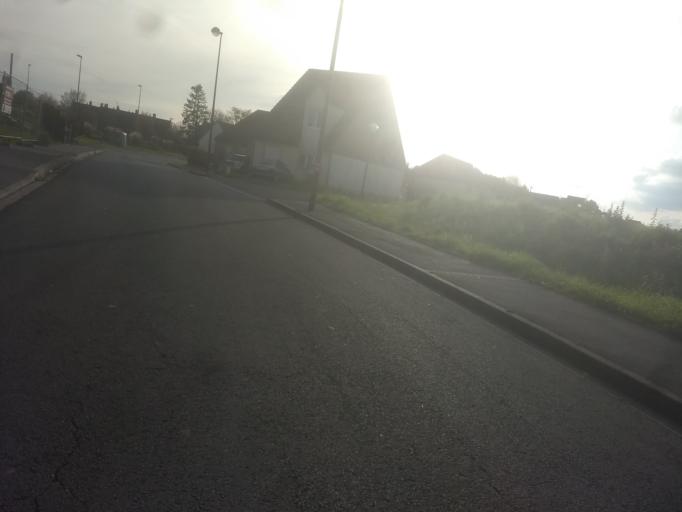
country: FR
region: Nord-Pas-de-Calais
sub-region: Departement du Pas-de-Calais
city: Arras
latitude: 50.2781
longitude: 2.7779
